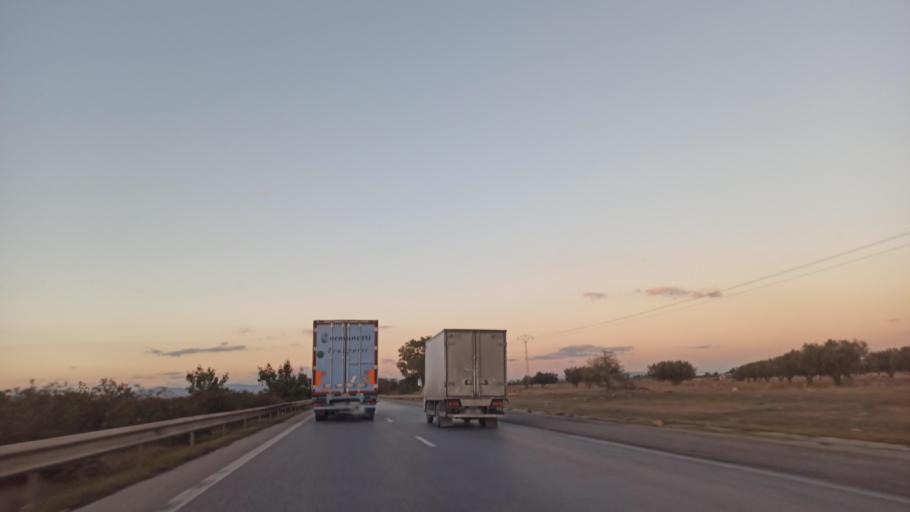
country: TN
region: Nabul
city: Al Hammamat
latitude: 36.2701
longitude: 10.4325
